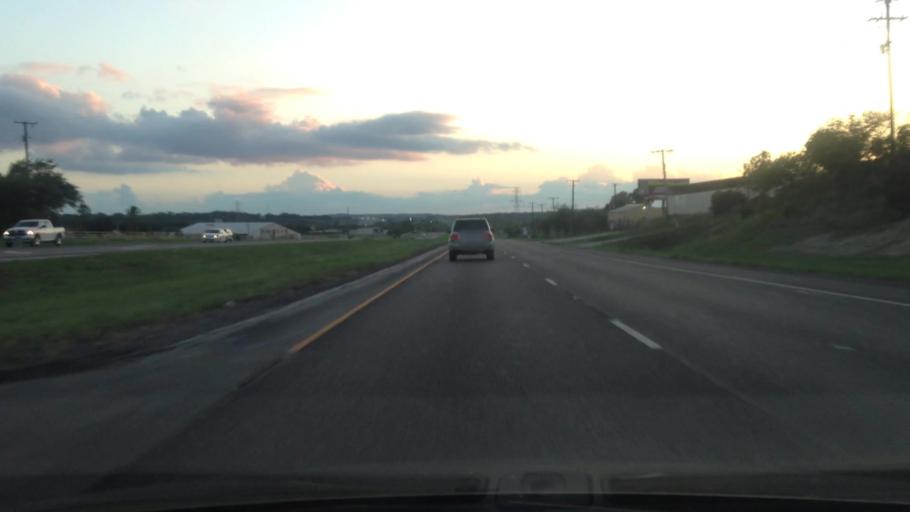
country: US
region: Texas
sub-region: Parker County
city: Aledo
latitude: 32.6030
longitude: -97.5621
